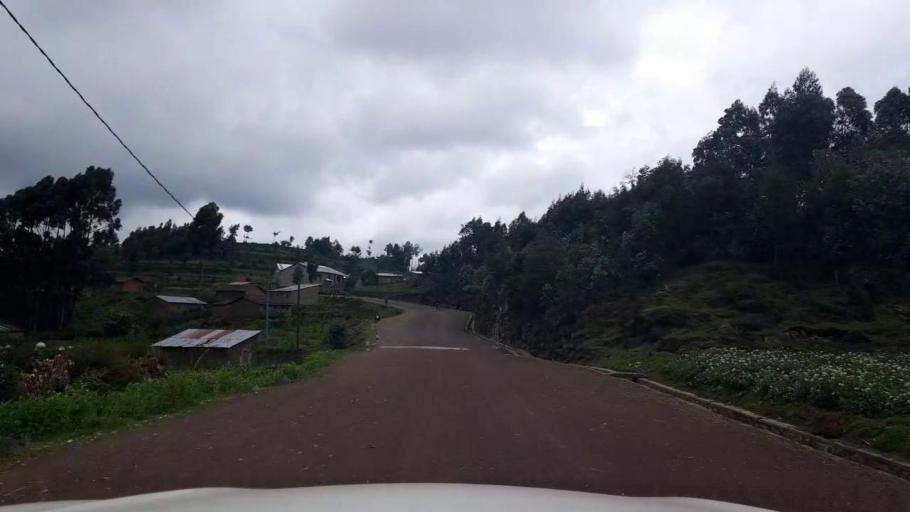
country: RW
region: Northern Province
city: Musanze
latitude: -1.5794
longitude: 29.4824
